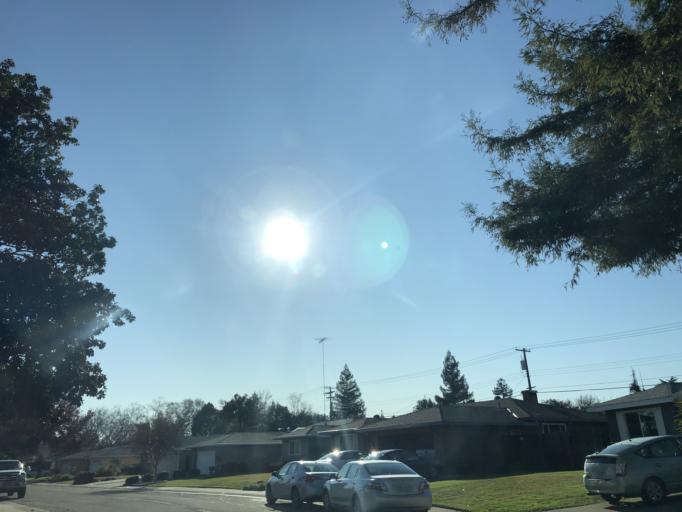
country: US
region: California
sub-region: Sacramento County
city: Rosemont
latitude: 38.5536
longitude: -121.4033
